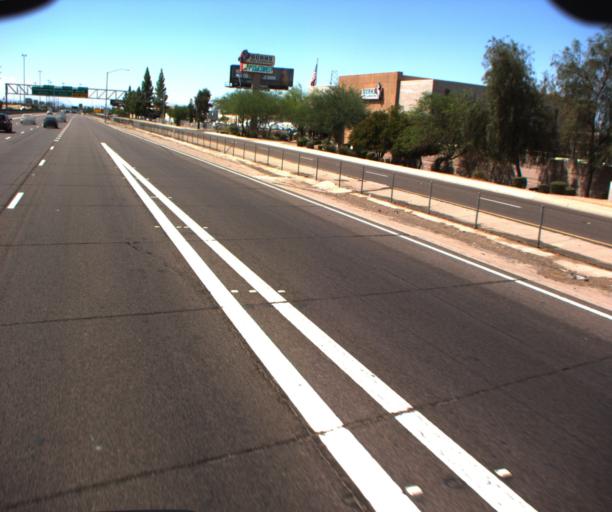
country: US
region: Arizona
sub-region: Maricopa County
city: Glendale
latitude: 33.6485
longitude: -112.1152
